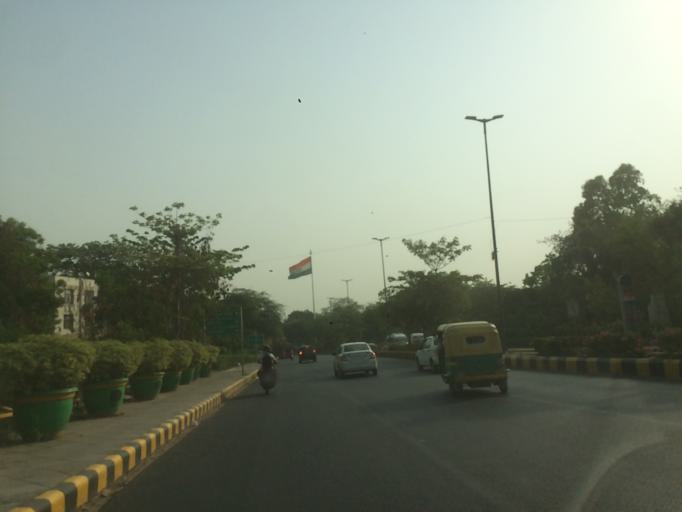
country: IN
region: NCT
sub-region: New Delhi
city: New Delhi
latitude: 28.5841
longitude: 77.1837
